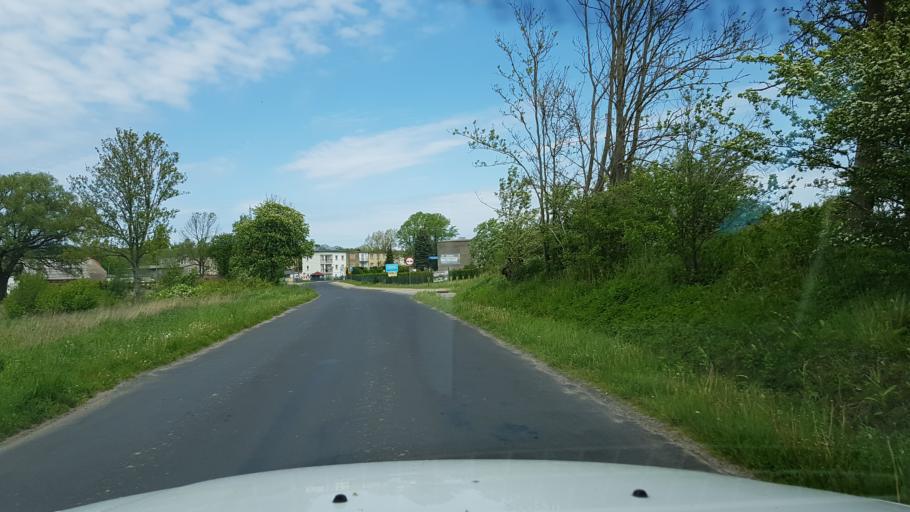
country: PL
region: West Pomeranian Voivodeship
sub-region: Powiat koszalinski
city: Mielno
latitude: 54.2475
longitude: 16.0096
